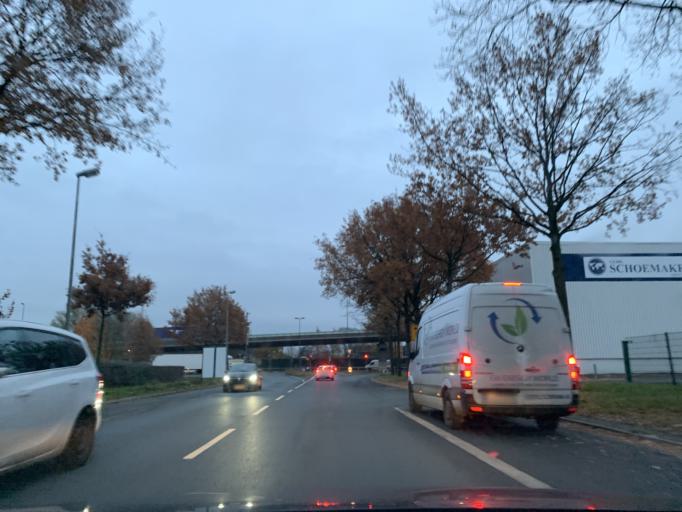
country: DE
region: Bremen
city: Bremen
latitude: 53.1053
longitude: 8.8003
